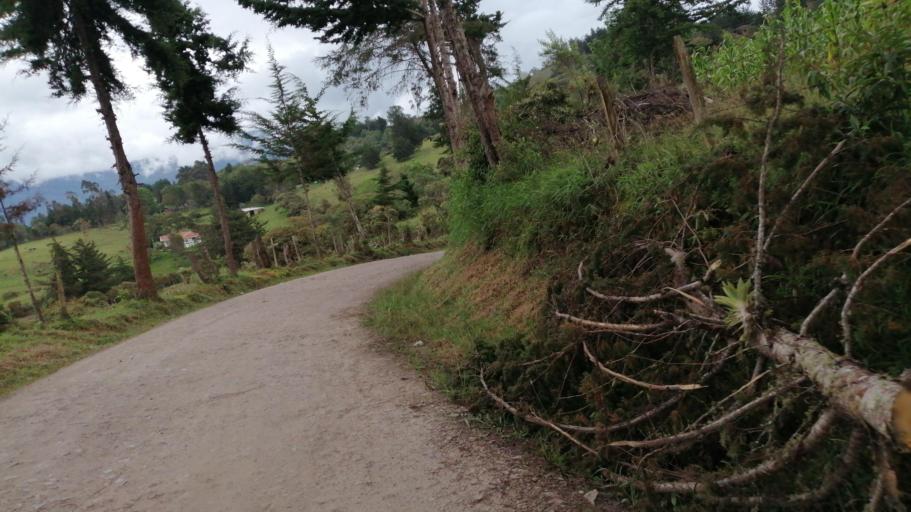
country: CO
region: Boyaca
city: Chinavita
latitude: 5.1337
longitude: -73.3963
